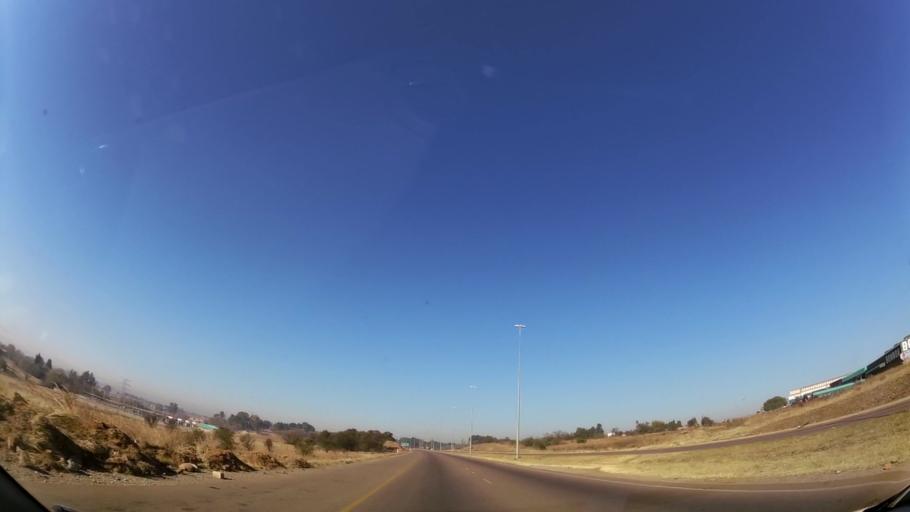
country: ZA
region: Gauteng
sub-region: City of Tshwane Metropolitan Municipality
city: Centurion
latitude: -25.8441
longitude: 28.1093
